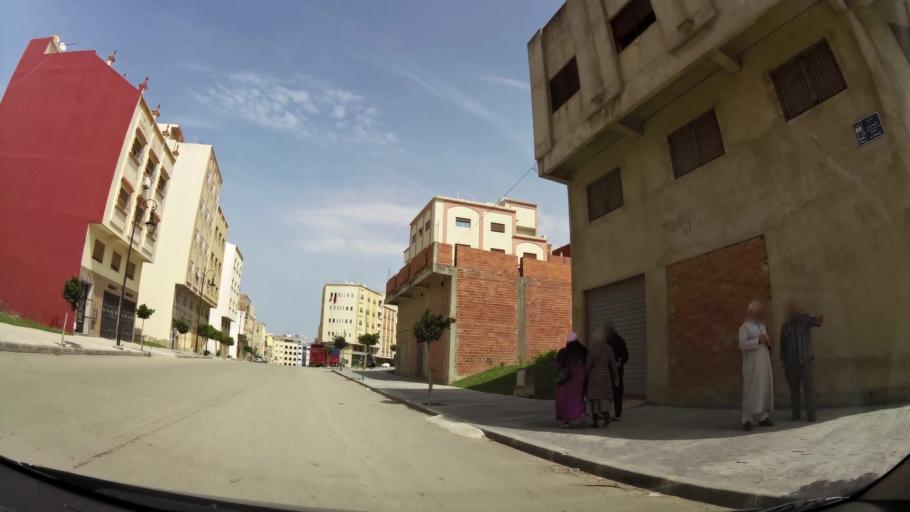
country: MA
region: Tanger-Tetouan
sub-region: Tanger-Assilah
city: Tangier
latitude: 35.7433
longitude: -5.8347
